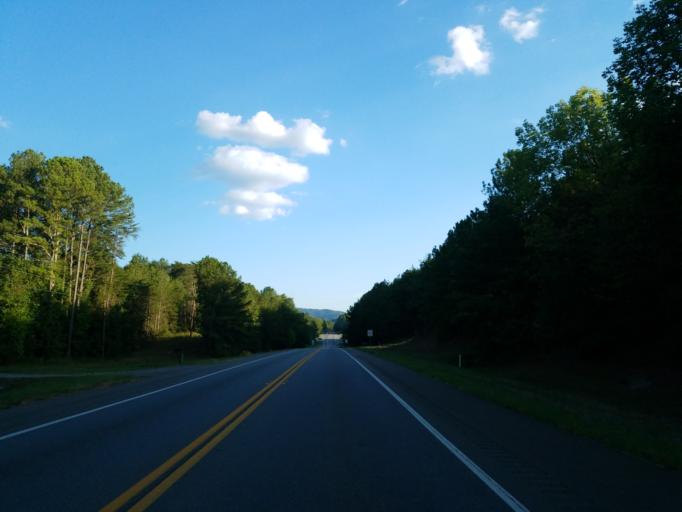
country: US
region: Georgia
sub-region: Murray County
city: Chatsworth
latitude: 34.5933
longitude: -84.7080
